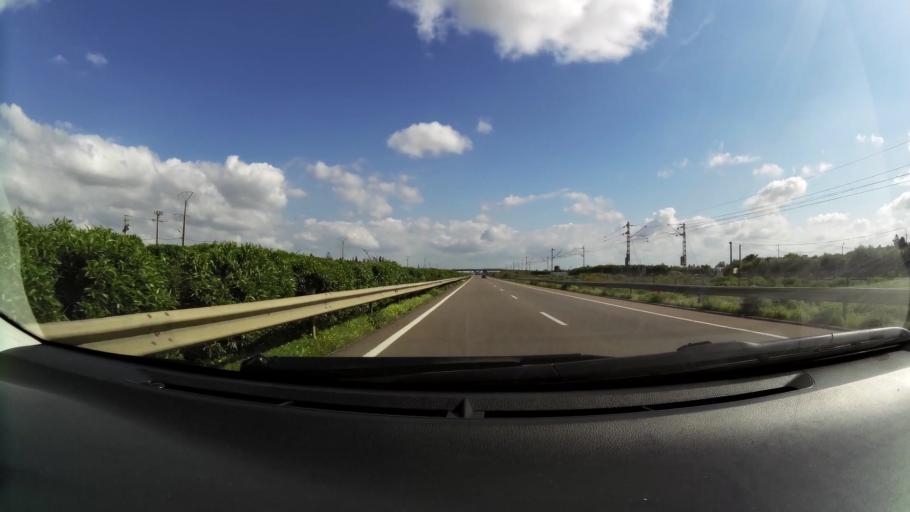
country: MA
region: Chaouia-Ouardigha
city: Nouaseur
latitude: 33.3388
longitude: -7.6116
